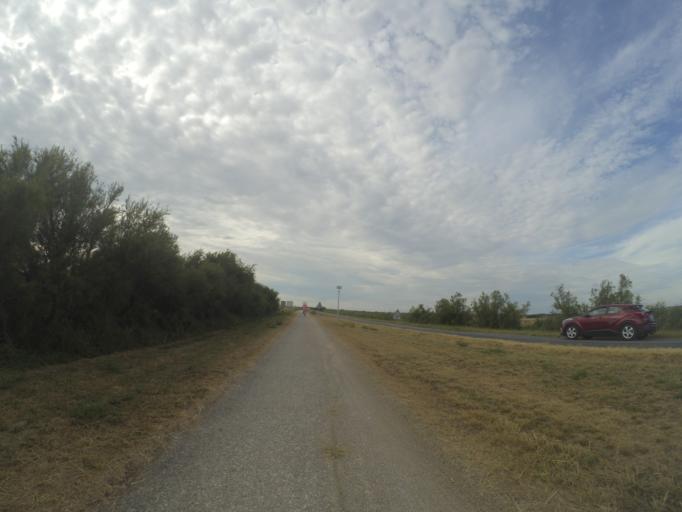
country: FR
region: Poitou-Charentes
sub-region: Departement de la Charente-Maritime
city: Meschers-sur-Gironde
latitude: 45.5386
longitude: -0.9059
